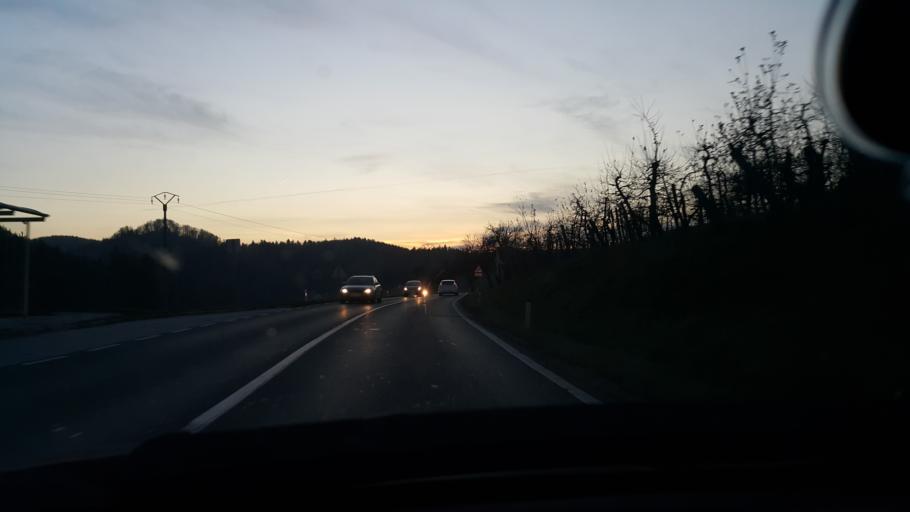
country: SI
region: Dobrna
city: Dobrna
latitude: 46.3223
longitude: 15.1828
